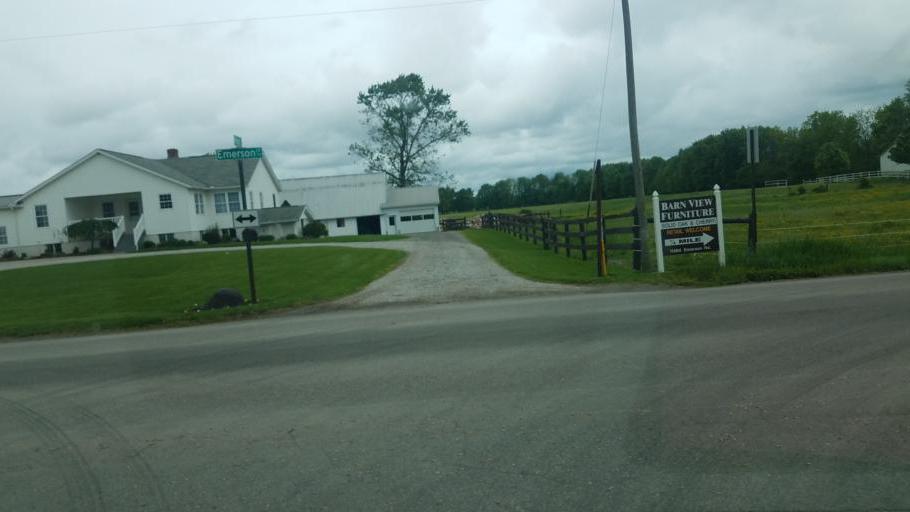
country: US
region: Ohio
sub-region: Wayne County
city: Apple Creek
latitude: 40.7412
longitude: -81.7850
